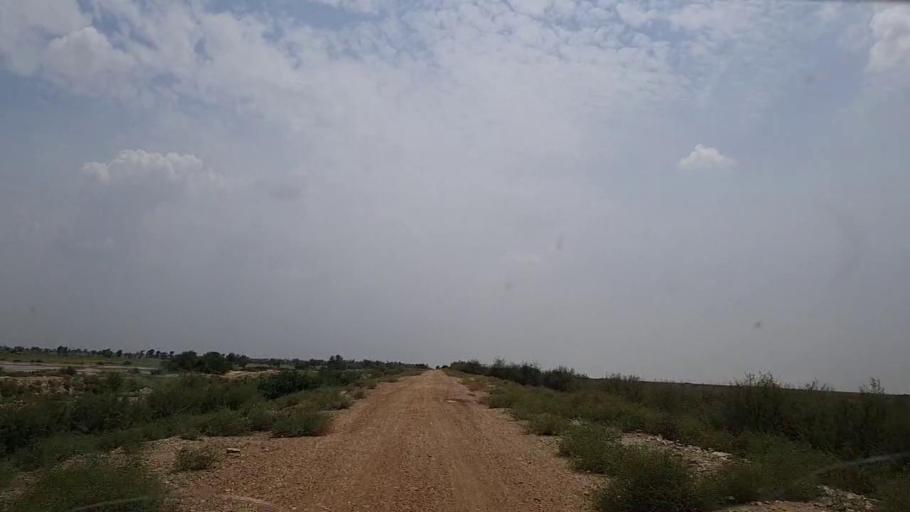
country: PK
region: Sindh
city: Phulji
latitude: 26.8199
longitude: 67.6118
